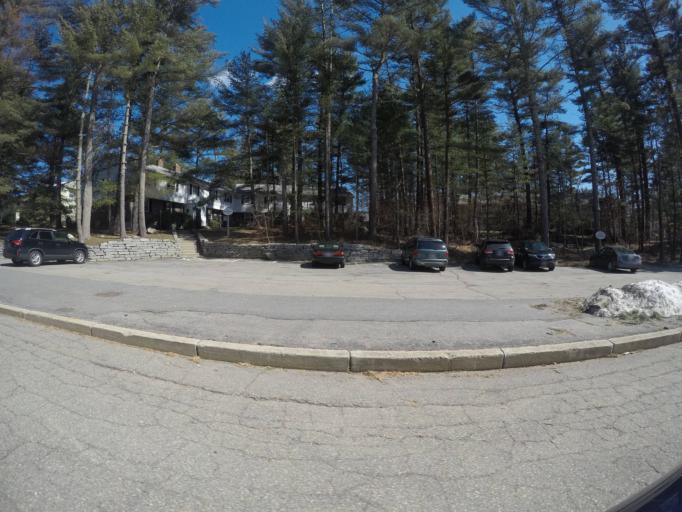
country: US
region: Massachusetts
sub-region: Bristol County
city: Easton
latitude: 42.0143
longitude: -71.1579
